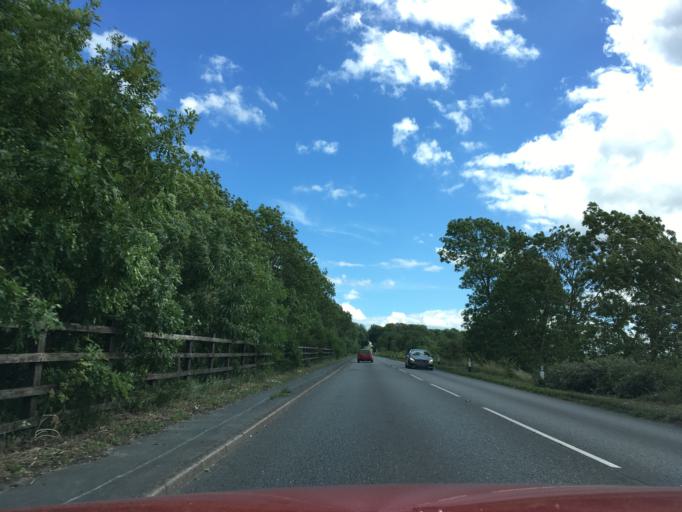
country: GB
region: England
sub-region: Nottinghamshire
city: East Bridgford
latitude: 52.9821
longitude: -0.9832
